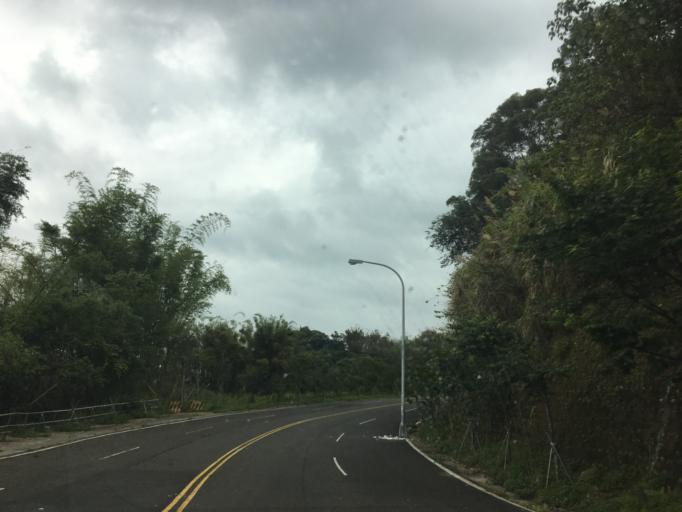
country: TW
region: Taiwan
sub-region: Taichung City
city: Taichung
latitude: 24.0634
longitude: 120.7235
